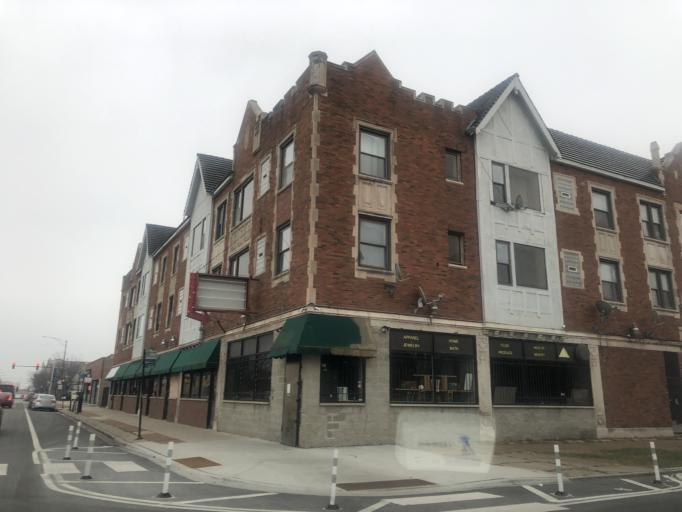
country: US
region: Illinois
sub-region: Cook County
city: Evergreen Park
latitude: 41.7512
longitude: -87.6114
